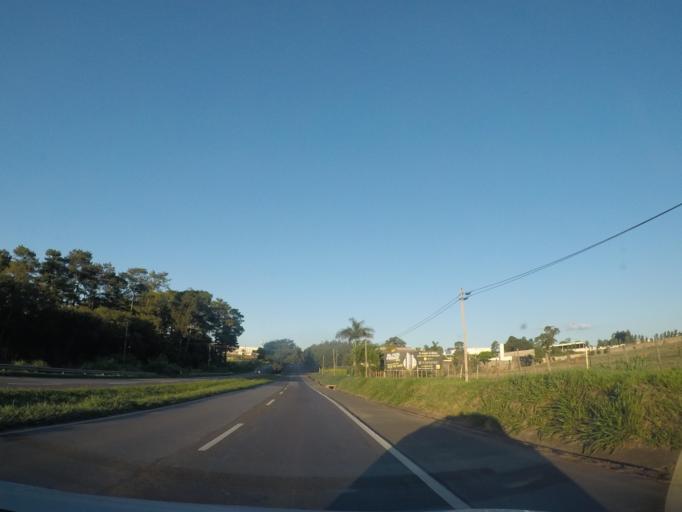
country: BR
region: Sao Paulo
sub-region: Sumare
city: Sumare
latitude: -22.7981
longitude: -47.2336
